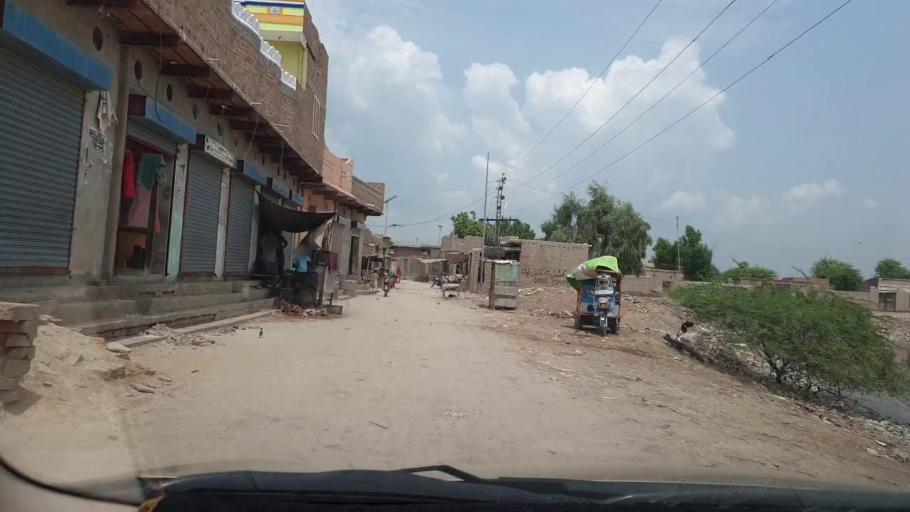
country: PK
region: Sindh
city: Larkana
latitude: 27.5602
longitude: 68.1235
